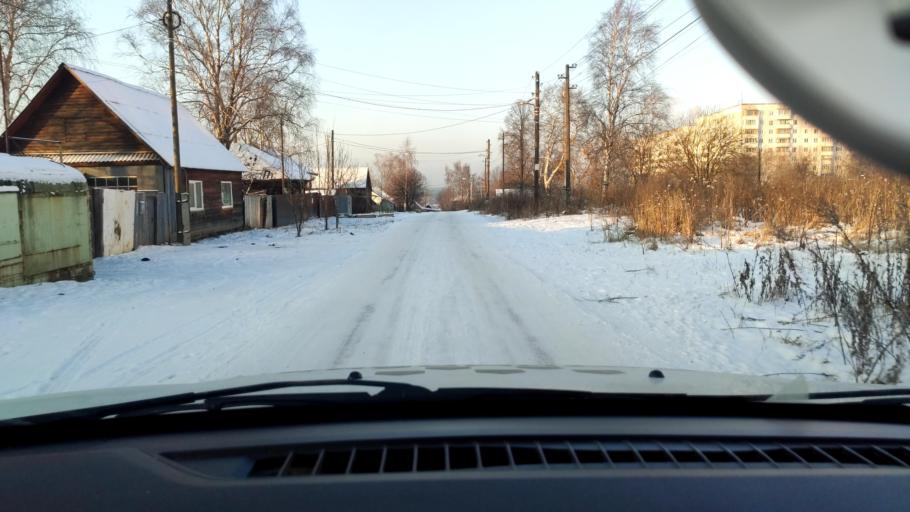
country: RU
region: Perm
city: Perm
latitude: 58.0290
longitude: 56.3204
